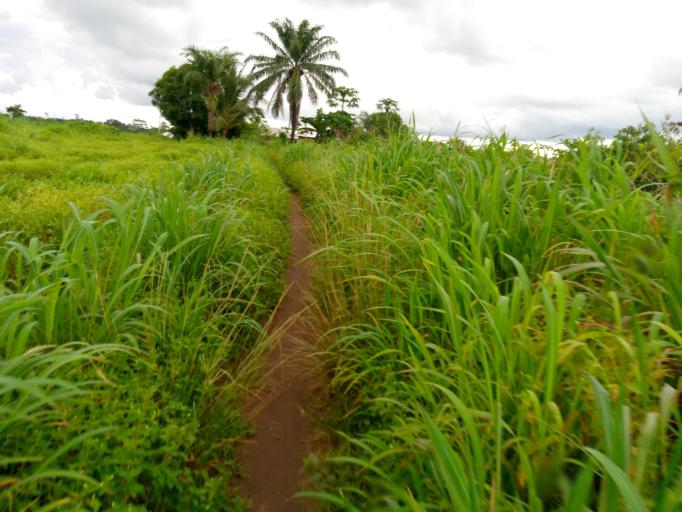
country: SL
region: Southern Province
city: Moyamba
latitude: 8.1527
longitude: -12.4417
